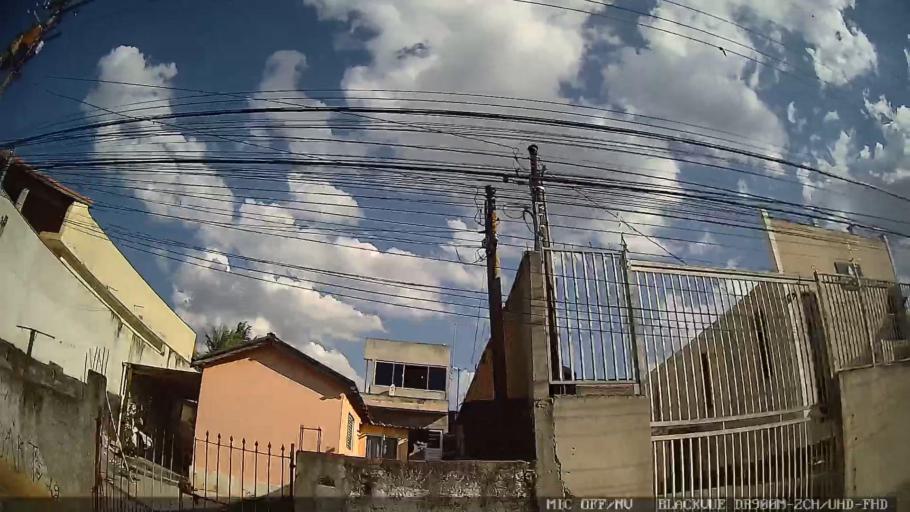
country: BR
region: Sao Paulo
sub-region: Ferraz De Vasconcelos
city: Ferraz de Vasconcelos
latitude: -23.5179
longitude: -46.4246
